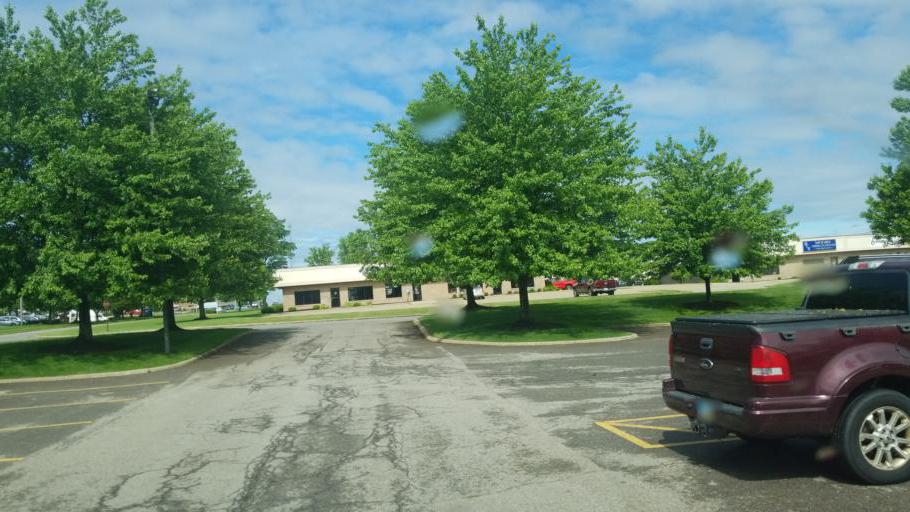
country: US
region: Ohio
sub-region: Wayne County
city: Wooster
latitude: 40.8436
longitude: -81.9436
